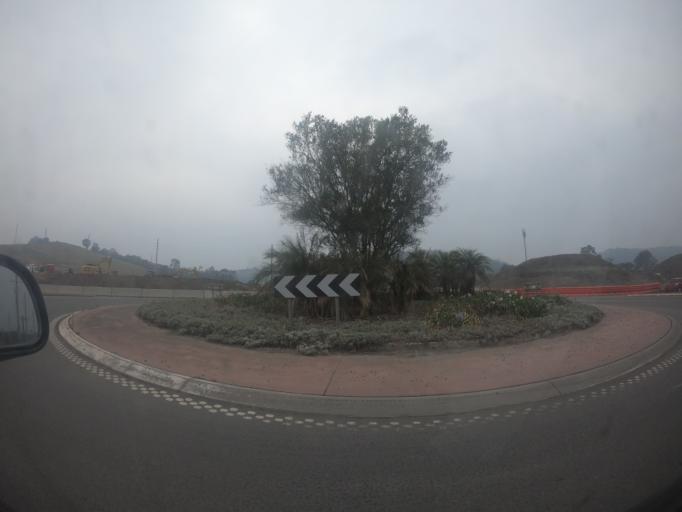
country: AU
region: New South Wales
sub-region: Shellharbour
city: Albion Park Rail
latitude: -34.5757
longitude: 150.8145
